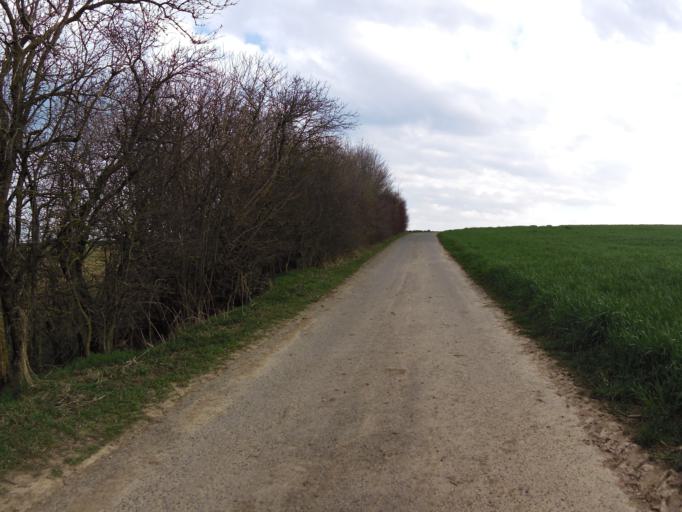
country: DE
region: Bavaria
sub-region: Regierungsbezirk Unterfranken
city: Buchbrunn
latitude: 49.7419
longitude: 10.1204
